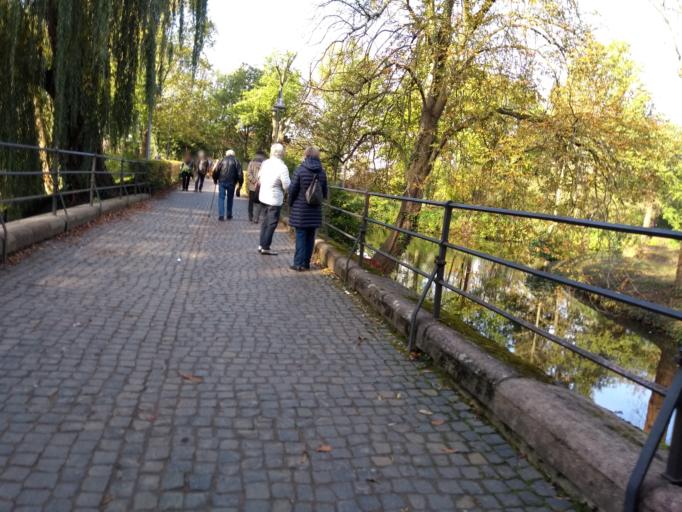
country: DE
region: North Rhine-Westphalia
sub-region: Regierungsbezirk Dusseldorf
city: Korschenbroich
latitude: 51.1819
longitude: 6.4807
